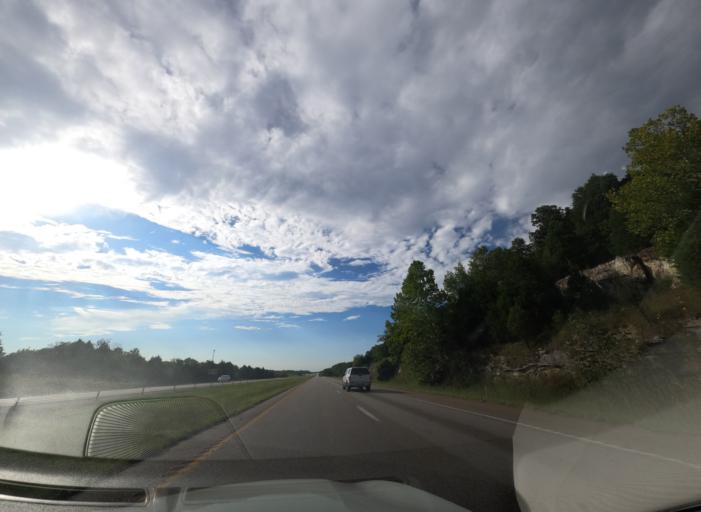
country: US
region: Missouri
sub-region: Sainte Genevieve County
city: Sainte Genevieve
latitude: 38.0231
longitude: -90.2367
